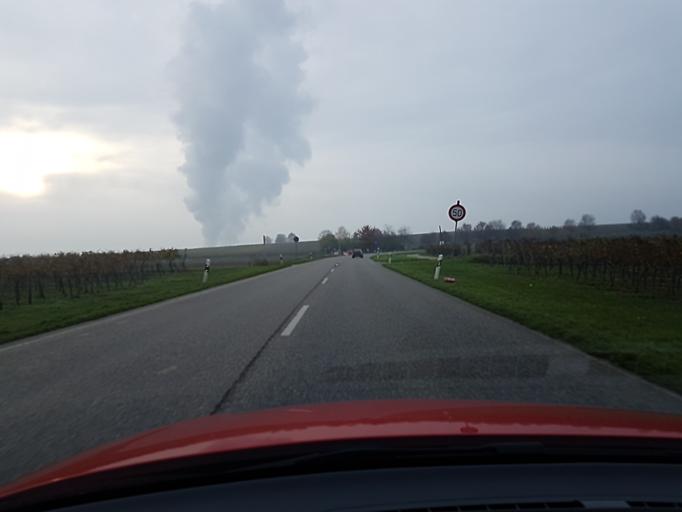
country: DE
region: Baden-Wuerttemberg
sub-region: Regierungsbezirk Stuttgart
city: Lauffen am Neckar
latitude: 49.0617
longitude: 9.1608
